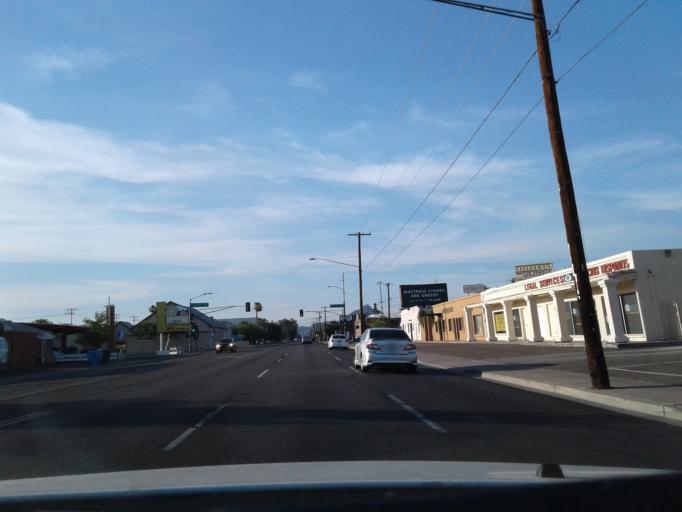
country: US
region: Arizona
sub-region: Maricopa County
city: Phoenix
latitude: 33.4720
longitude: -112.0302
